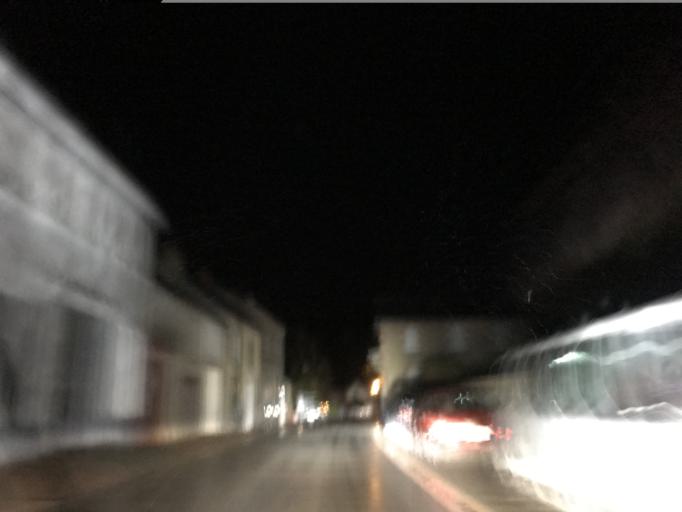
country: FR
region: Auvergne
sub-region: Departement de l'Allier
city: Saint-Yorre
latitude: 46.0614
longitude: 3.5131
